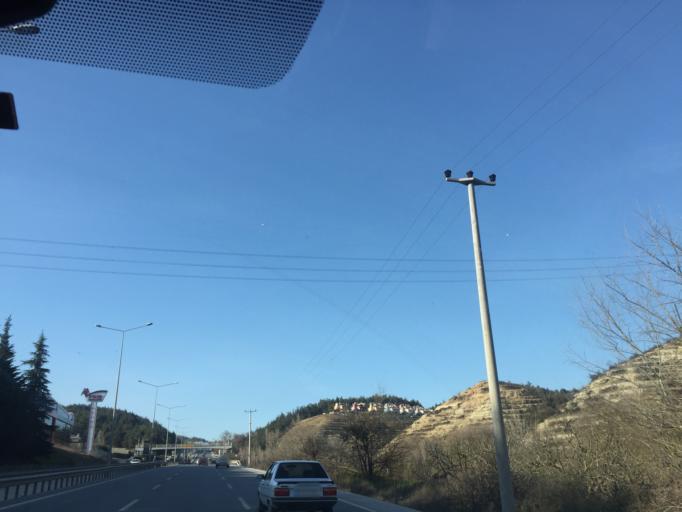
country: TR
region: Bursa
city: Niluefer
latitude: 40.3099
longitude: 28.9367
